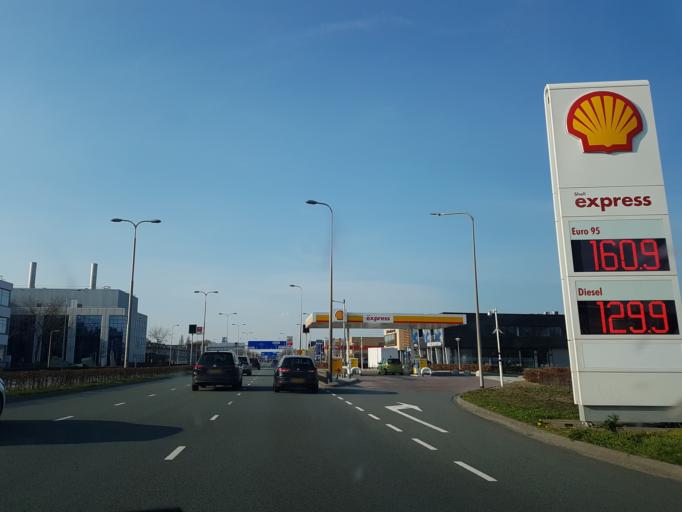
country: NL
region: Overijssel
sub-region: Gemeente Zwolle
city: Zwolle
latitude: 52.5187
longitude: 6.1187
